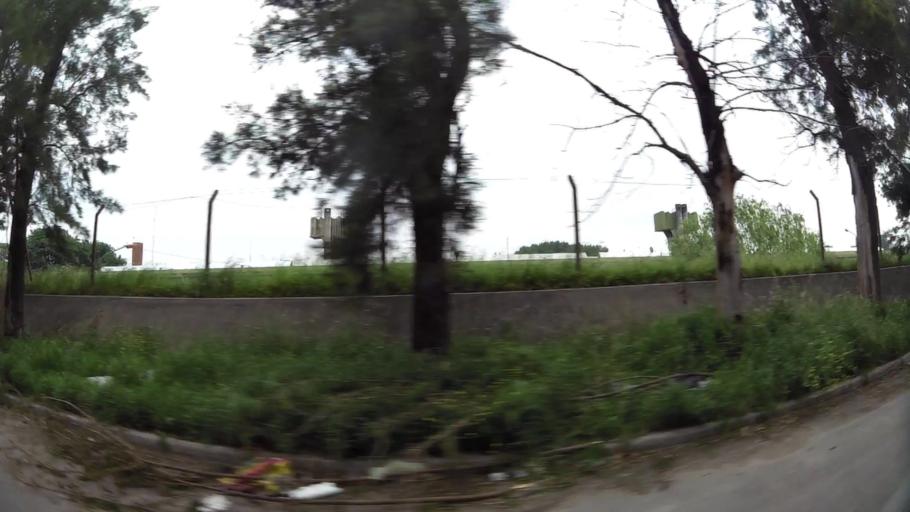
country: AR
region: Buenos Aires
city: San Justo
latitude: -34.6946
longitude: -58.5793
